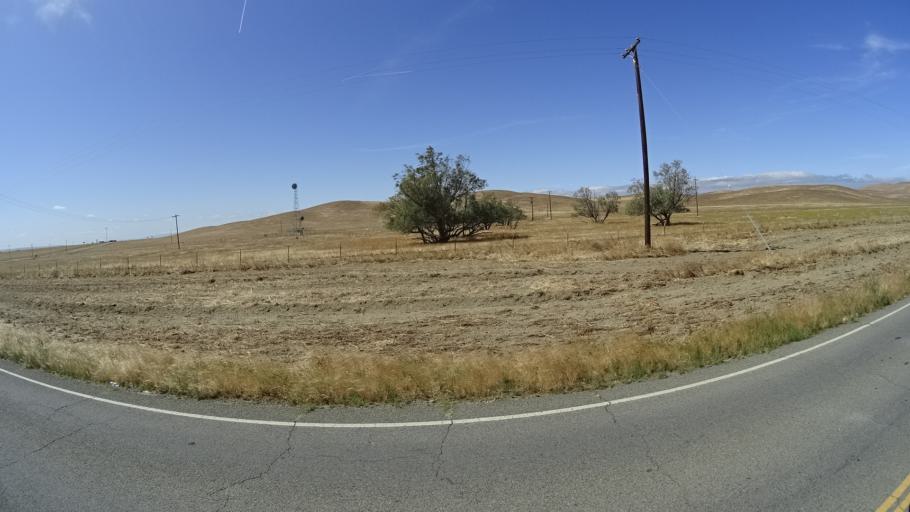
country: US
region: California
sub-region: Kings County
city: Avenal
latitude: 35.9032
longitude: -120.0551
